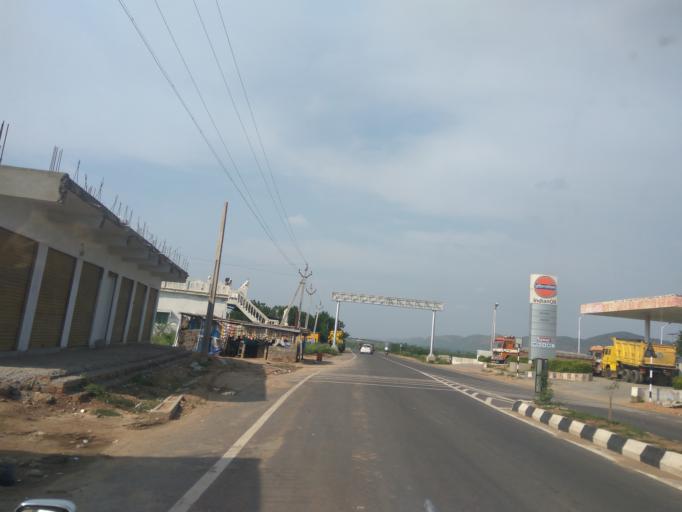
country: IN
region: Andhra Pradesh
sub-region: Prakasam
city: Markapur
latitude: 15.7961
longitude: 79.2572
